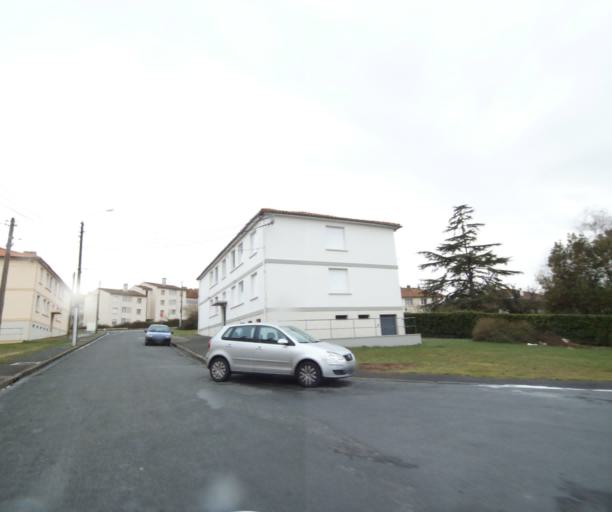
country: FR
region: Poitou-Charentes
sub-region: Departement des Deux-Sevres
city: Niort
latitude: 46.3340
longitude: -0.4473
